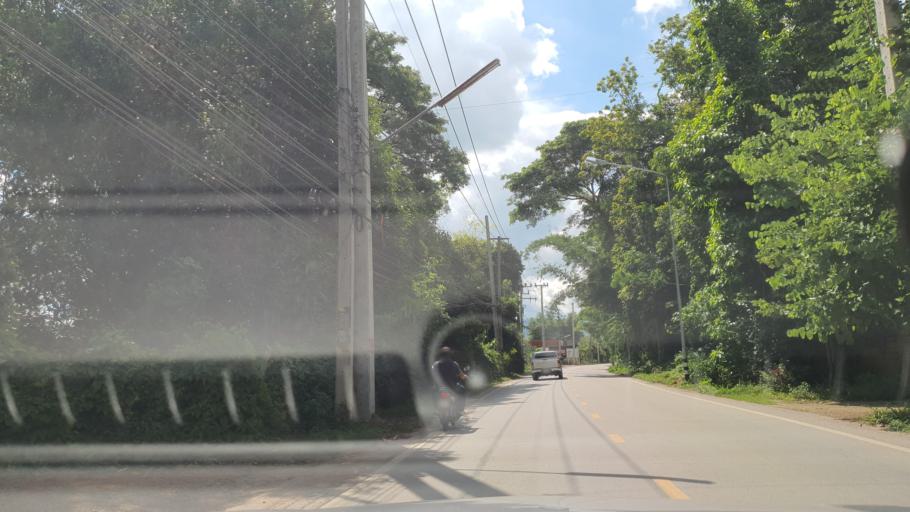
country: TH
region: Chiang Mai
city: Mae Wang
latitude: 18.6001
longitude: 98.8127
